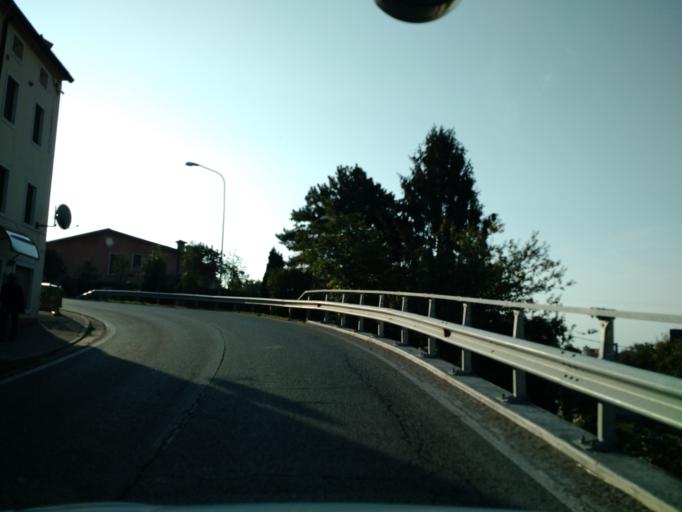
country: IT
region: Veneto
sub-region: Provincia di Vicenza
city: Salcedo
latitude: 45.7733
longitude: 11.5620
